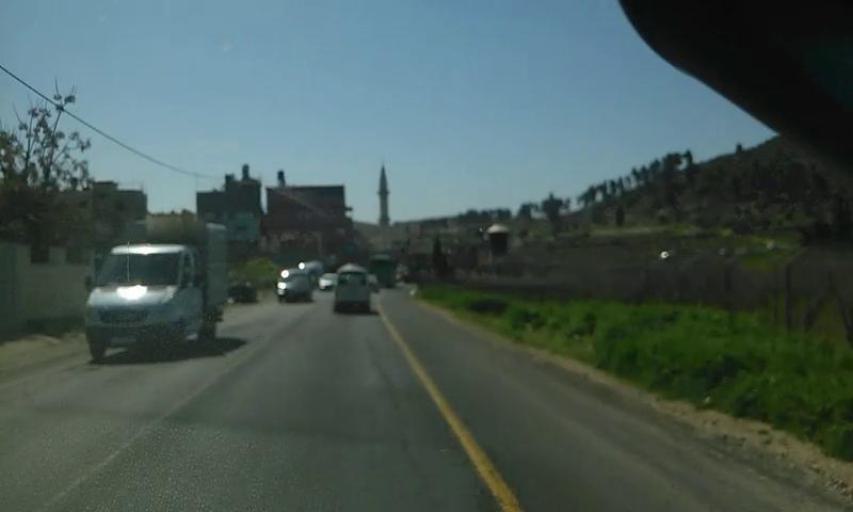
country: PS
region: West Bank
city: Shuyukh al `Arrub
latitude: 31.6263
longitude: 35.1328
